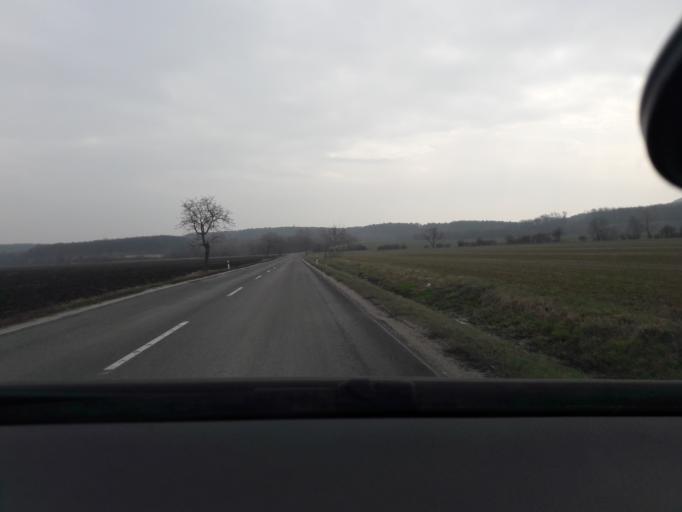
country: SK
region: Trnavsky
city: Smolenice
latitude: 48.4885
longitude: 17.4237
